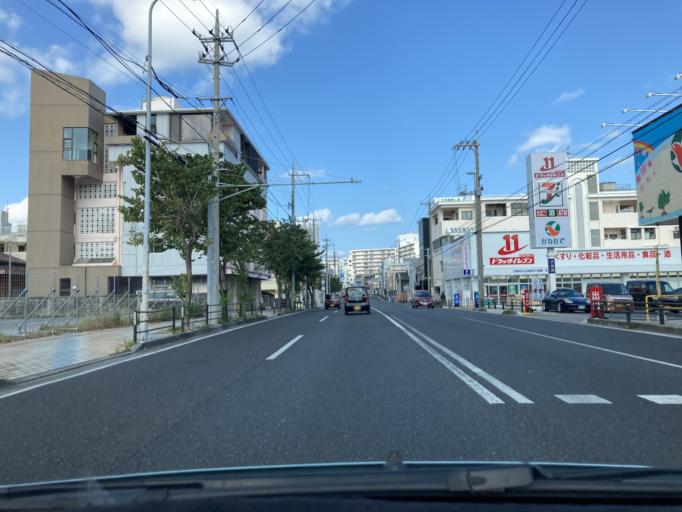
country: JP
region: Okinawa
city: Tomigusuku
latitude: 26.1979
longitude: 127.6892
